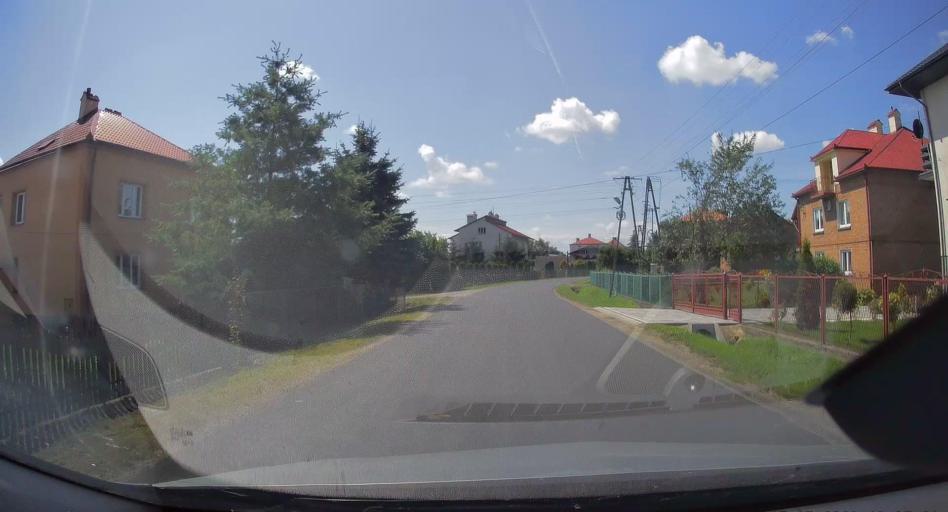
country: PL
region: Subcarpathian Voivodeship
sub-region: Powiat przemyski
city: Medyka
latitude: 49.8310
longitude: 22.8746
